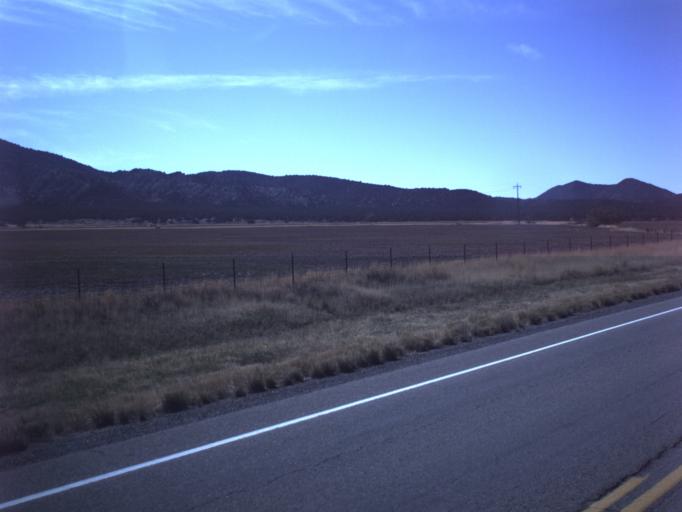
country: US
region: Utah
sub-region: Juab County
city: Nephi
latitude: 39.4677
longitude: -111.8982
